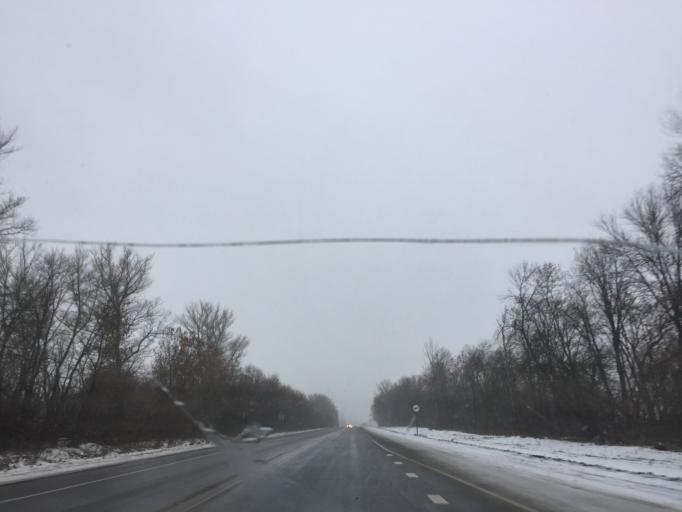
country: RU
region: Tula
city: Plavsk
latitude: 53.7313
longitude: 37.3076
